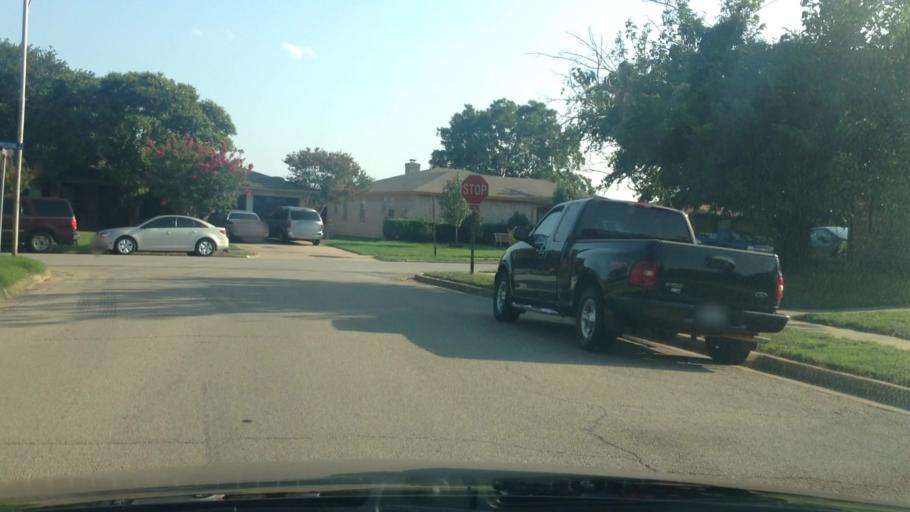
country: US
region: Texas
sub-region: Tarrant County
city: Edgecliff Village
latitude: 32.6505
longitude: -97.3459
